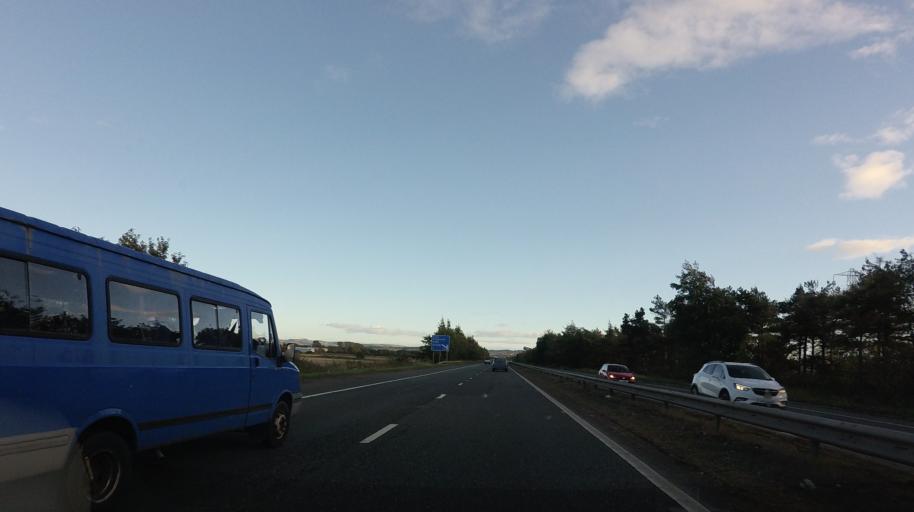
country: GB
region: Scotland
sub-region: Falkirk
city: Falkirk
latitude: 56.0268
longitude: -3.7609
